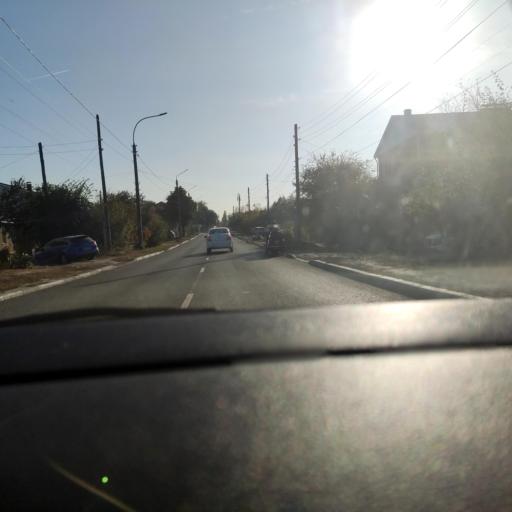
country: RU
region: Voronezj
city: Voronezh
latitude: 51.6324
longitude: 39.1681
